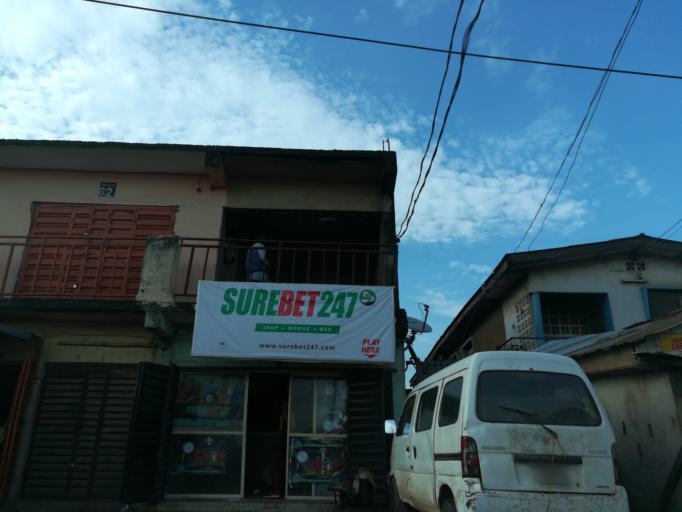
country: NG
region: Lagos
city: Oshodi
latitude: 6.5564
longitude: 3.3439
